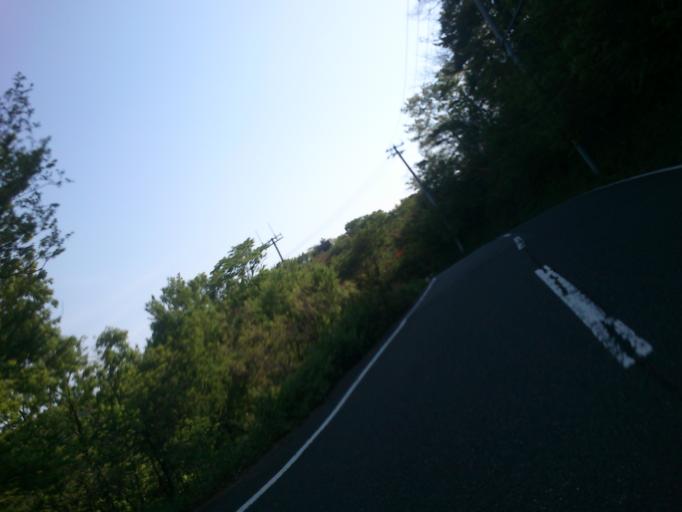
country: JP
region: Kyoto
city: Miyazu
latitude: 35.7226
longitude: 135.1873
